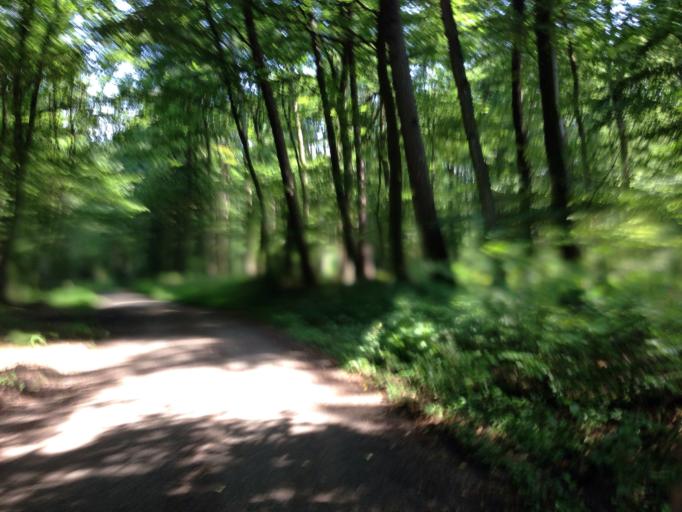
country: DE
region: Hesse
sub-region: Regierungsbezirk Darmstadt
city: Dietzenbach
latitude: 50.0182
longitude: 8.7437
